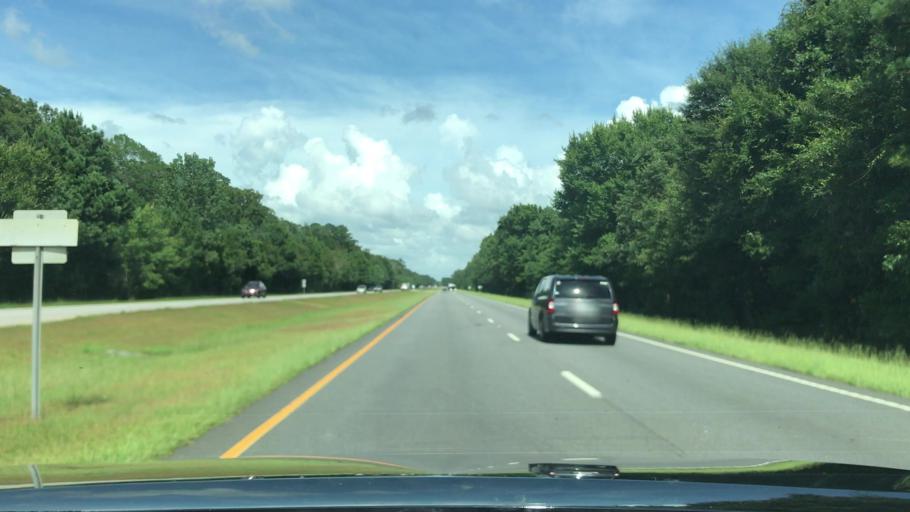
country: US
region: South Carolina
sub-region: Jasper County
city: Hardeeville
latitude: 32.3082
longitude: -81.0021
